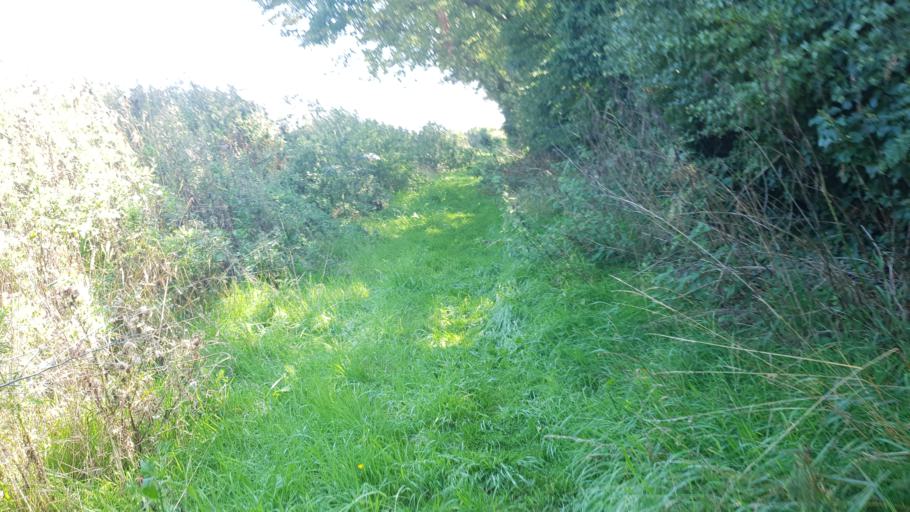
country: GB
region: England
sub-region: Essex
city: Colchester
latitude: 51.9237
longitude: 0.9482
